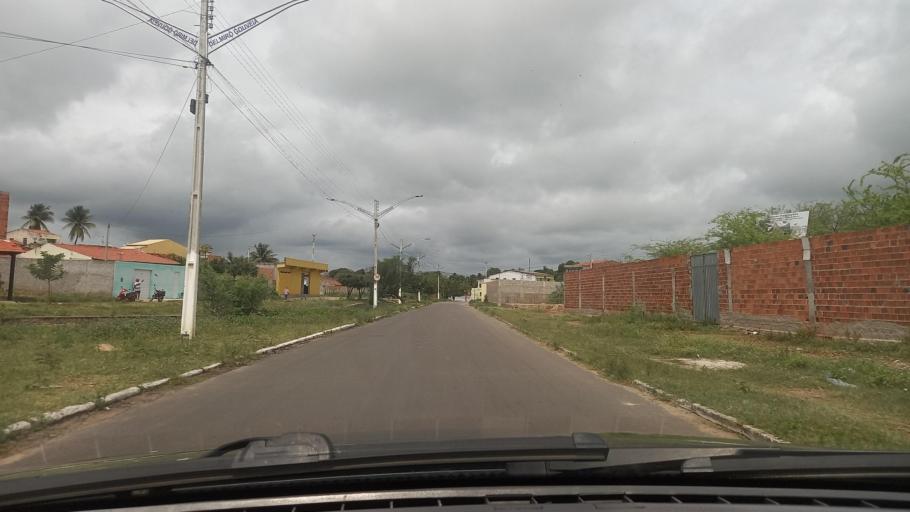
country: BR
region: Alagoas
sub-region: Delmiro Gouveia
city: Delmiro Gouveia
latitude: -9.3891
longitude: -38.0002
